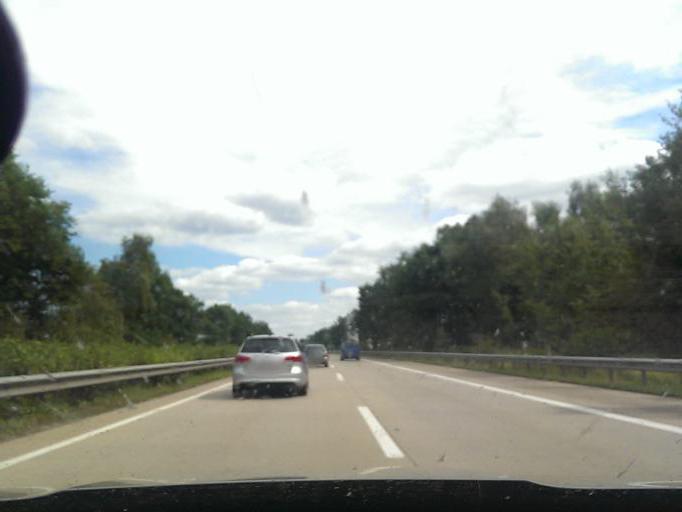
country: DE
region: Lower Saxony
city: Walsrode
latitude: 52.8122
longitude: 9.6236
